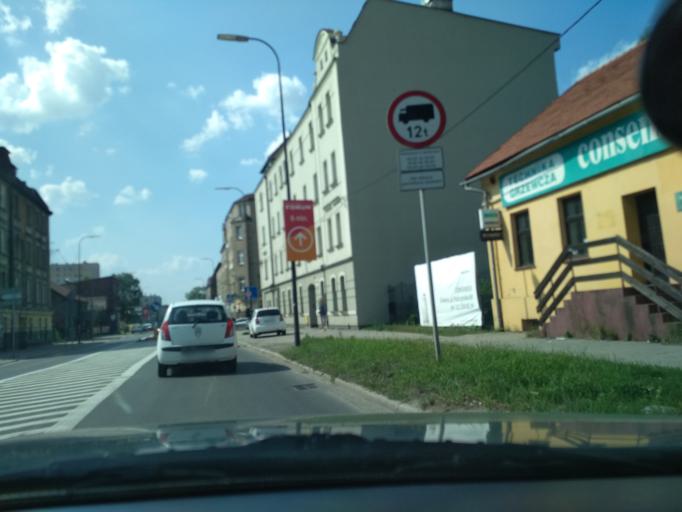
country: PL
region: Silesian Voivodeship
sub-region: Gliwice
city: Gliwice
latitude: 50.2858
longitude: 18.6762
